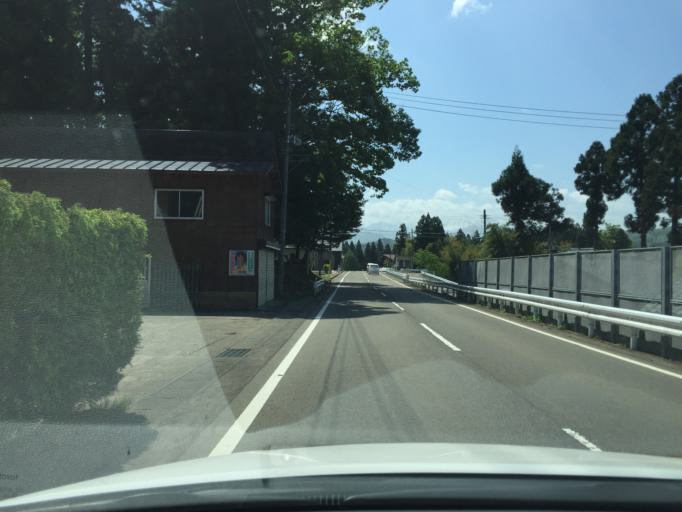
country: JP
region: Niigata
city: Tochio-honcho
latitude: 37.5547
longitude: 139.0784
